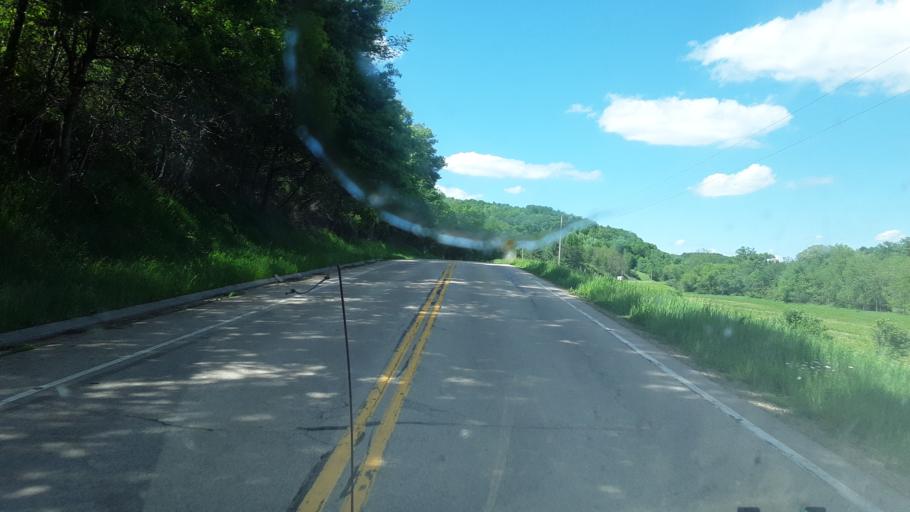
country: US
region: Wisconsin
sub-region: Richland County
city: Richland Center
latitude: 43.4596
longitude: -90.2140
